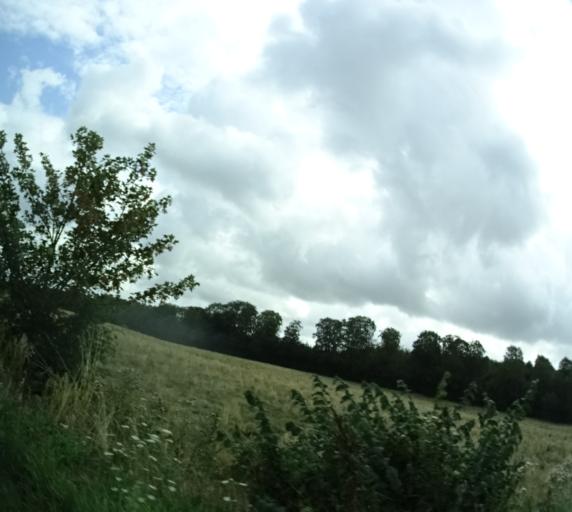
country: DK
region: Central Jutland
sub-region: Syddjurs Kommune
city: Ryomgard
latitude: 56.4009
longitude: 10.5193
